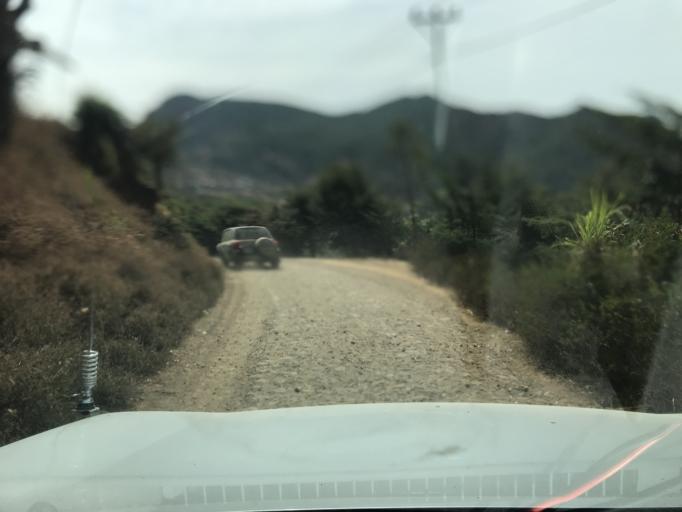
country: TL
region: Ainaro
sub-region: Ainaro
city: Ainaro
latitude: -8.8981
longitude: 125.5182
